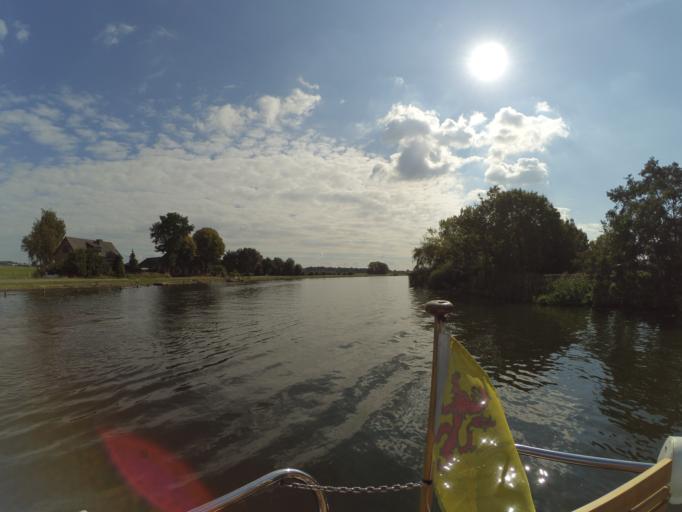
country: NL
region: North Holland
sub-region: Gemeente Amsterdam
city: Driemond
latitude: 52.2685
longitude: 5.0263
